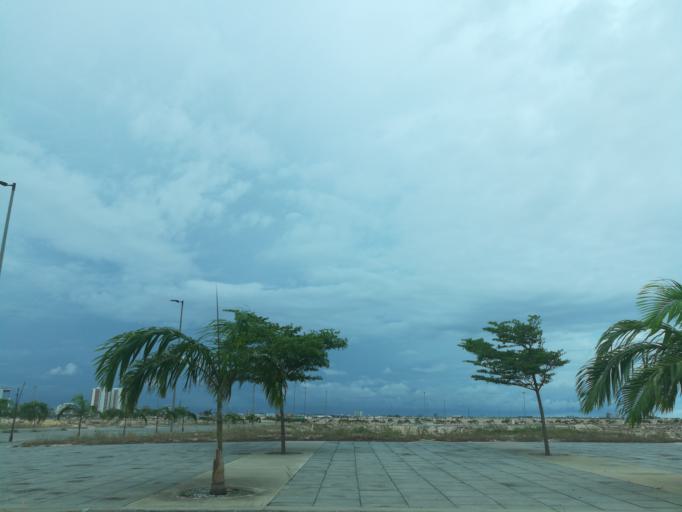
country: NG
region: Lagos
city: Ikoyi
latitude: 6.4112
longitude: 3.4172
